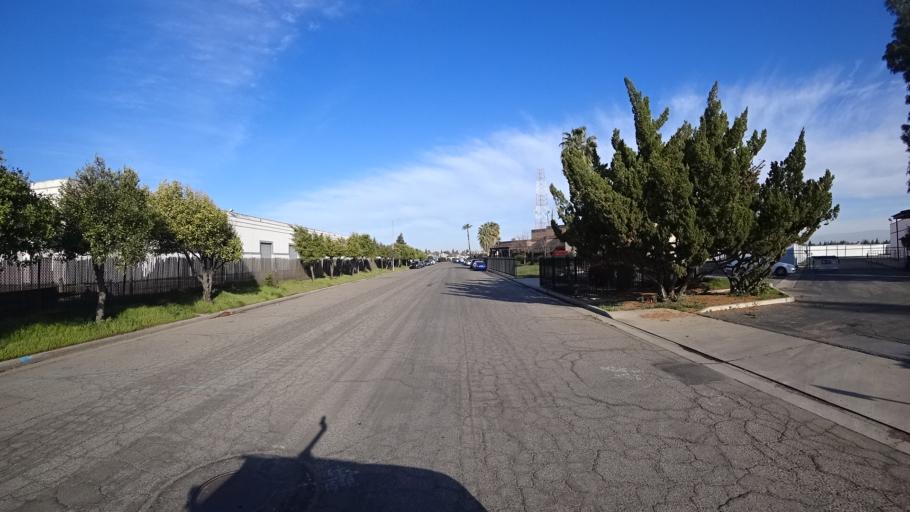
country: US
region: California
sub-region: Fresno County
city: West Park
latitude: 36.8149
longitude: -119.8806
